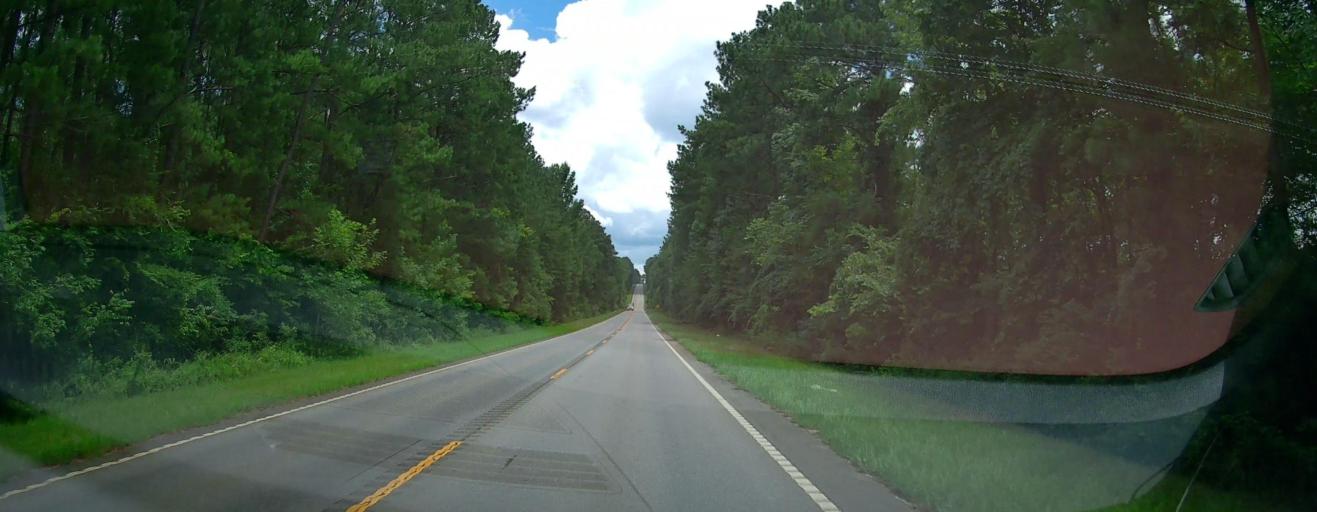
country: US
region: Georgia
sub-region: Pulaski County
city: Hawkinsville
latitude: 32.3836
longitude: -83.5526
